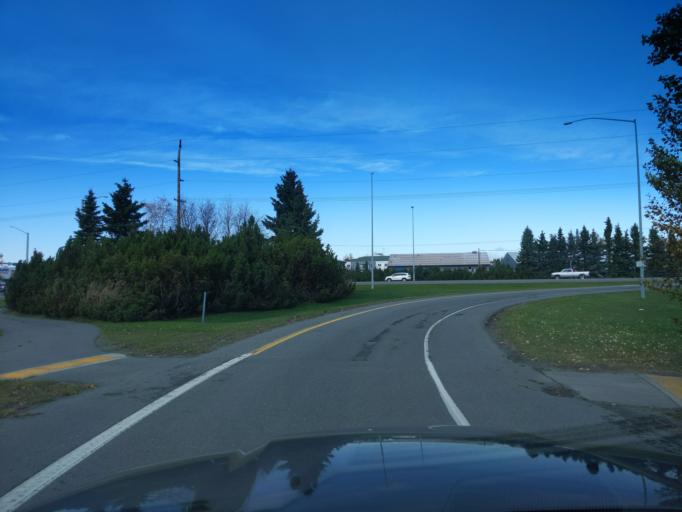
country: US
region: Alaska
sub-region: Anchorage Municipality
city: Anchorage
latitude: 61.1729
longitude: -149.9421
